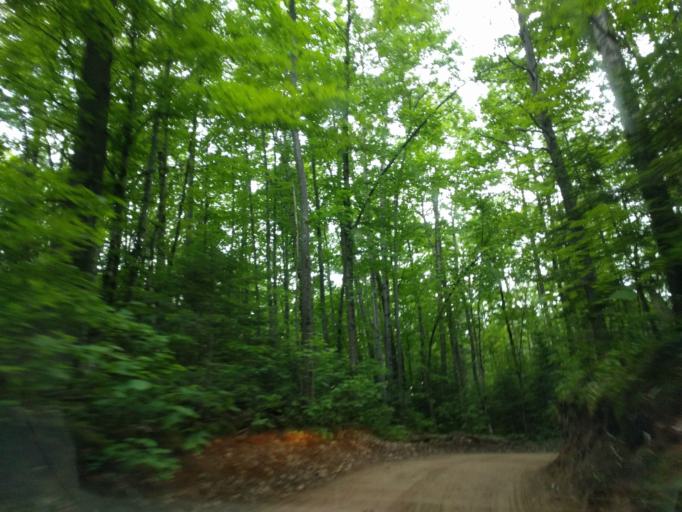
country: US
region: Michigan
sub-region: Marquette County
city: Trowbridge Park
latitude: 46.6000
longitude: -87.4974
